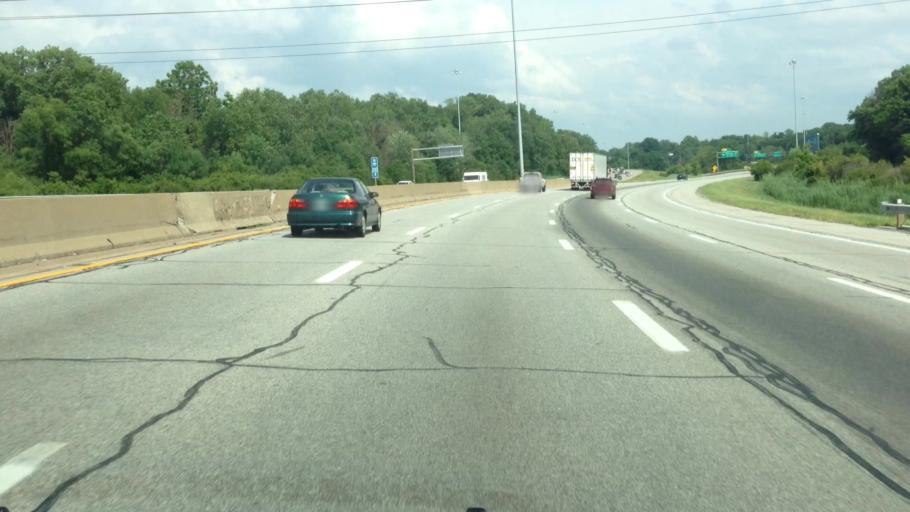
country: US
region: Ohio
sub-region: Cuyahoga County
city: Brooklyn
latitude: 41.4489
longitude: -81.7499
